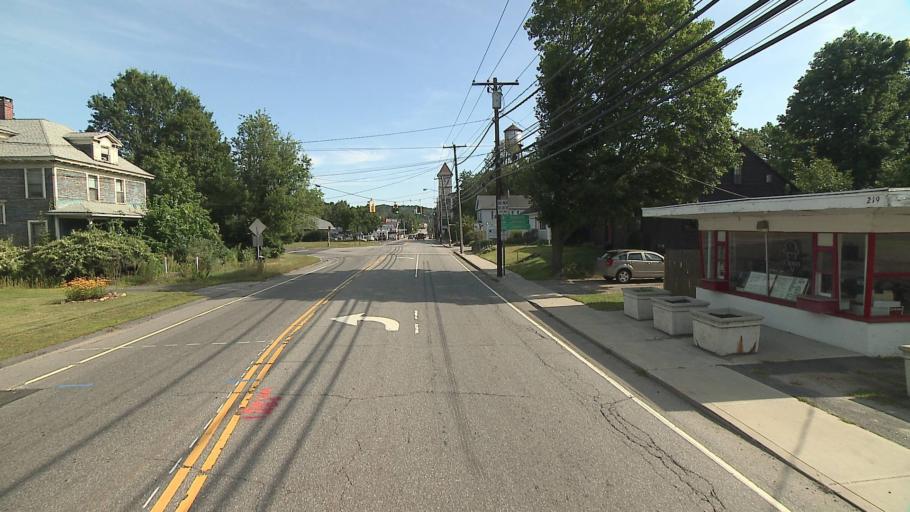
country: US
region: Connecticut
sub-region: Litchfield County
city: Thomaston
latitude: 41.6679
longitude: -73.0788
